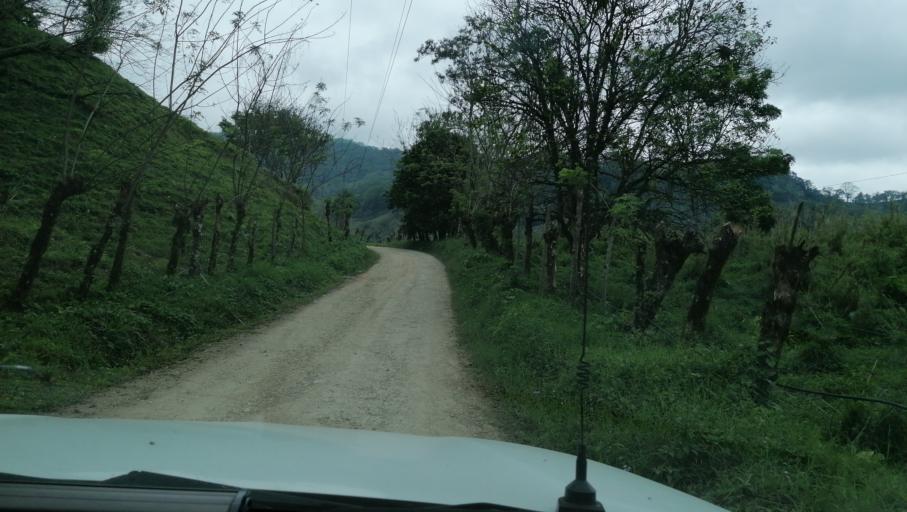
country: MX
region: Chiapas
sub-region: Ocotepec
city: San Pablo Huacano
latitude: 17.2739
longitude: -93.2377
